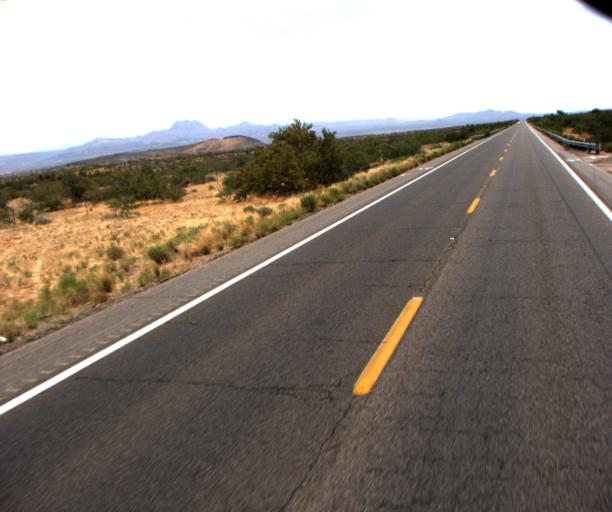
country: US
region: Arizona
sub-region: Gila County
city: Peridot
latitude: 33.3180
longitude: -110.5287
